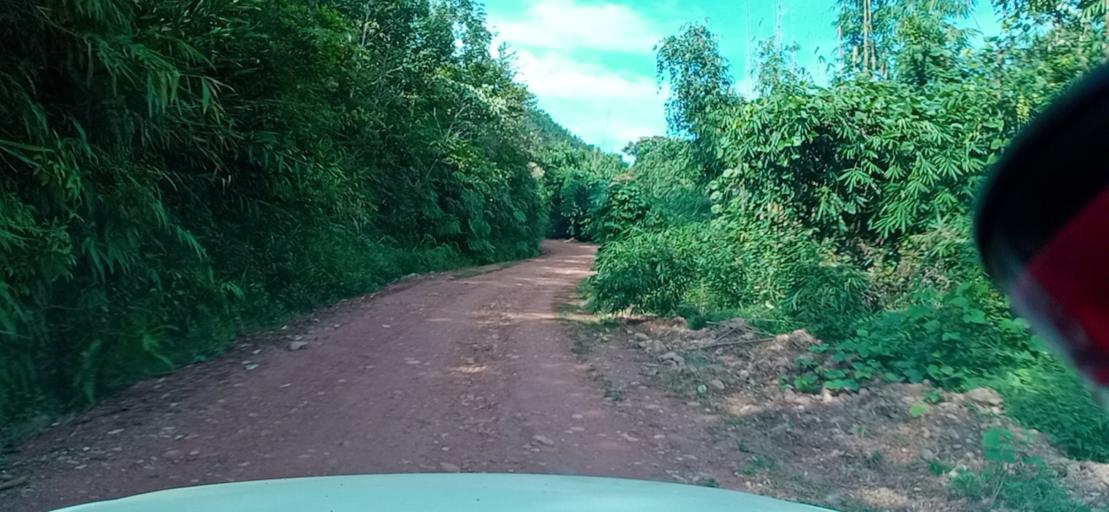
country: TH
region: Changwat Bueng Kan
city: Pak Khat
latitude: 18.6663
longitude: 103.1993
